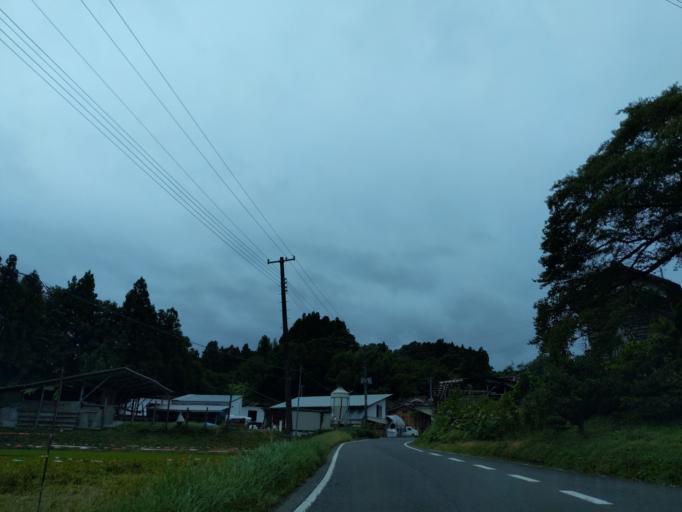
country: JP
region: Fukushima
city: Miharu
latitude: 37.3812
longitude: 140.5282
